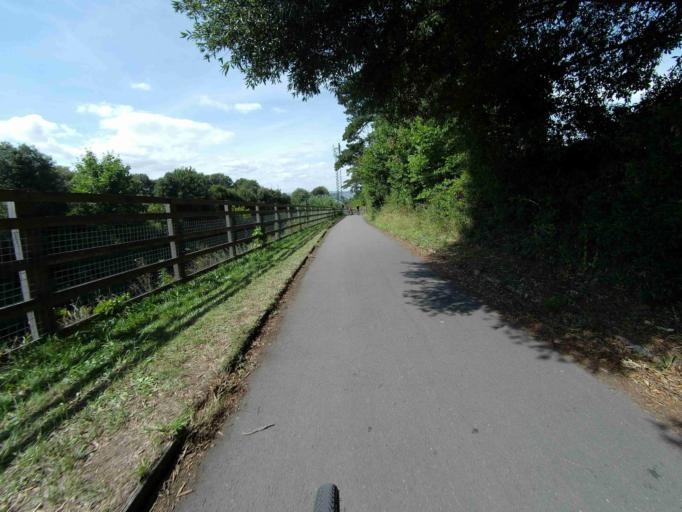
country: GB
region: England
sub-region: Devon
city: Starcross
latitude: 50.6497
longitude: -3.4321
